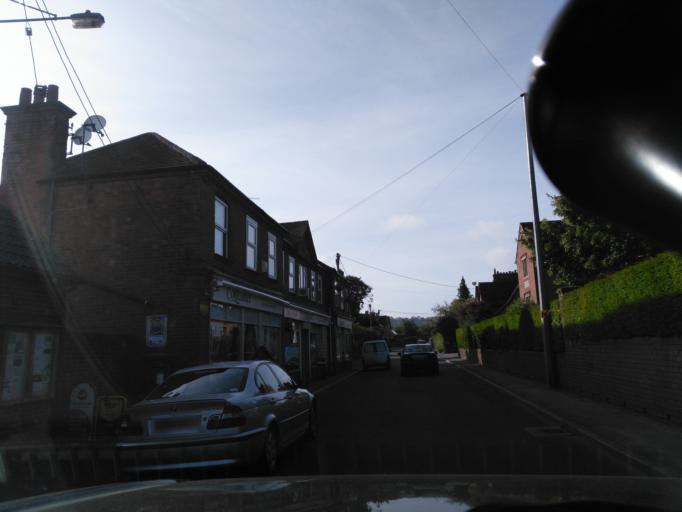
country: GB
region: England
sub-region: Wiltshire
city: Market Lavington
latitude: 51.2824
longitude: -1.9984
